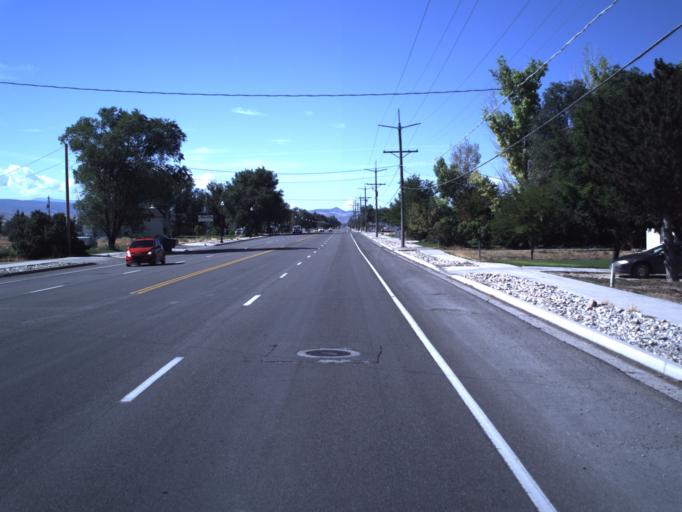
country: US
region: Utah
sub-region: Sanpete County
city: Centerfield
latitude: 39.1364
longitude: -111.8191
